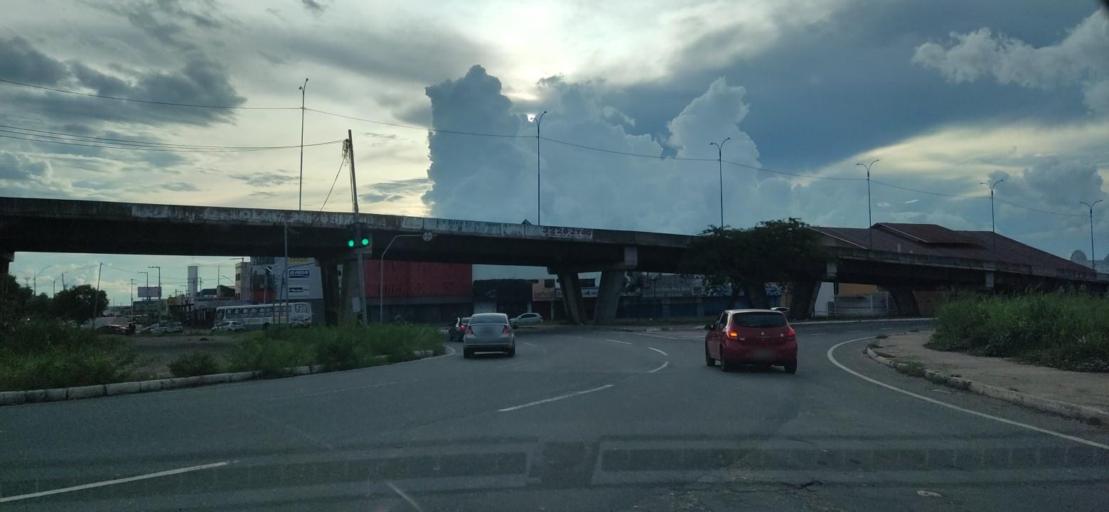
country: BR
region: Piaui
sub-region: Teresina
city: Teresina
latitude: -5.1227
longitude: -42.7950
